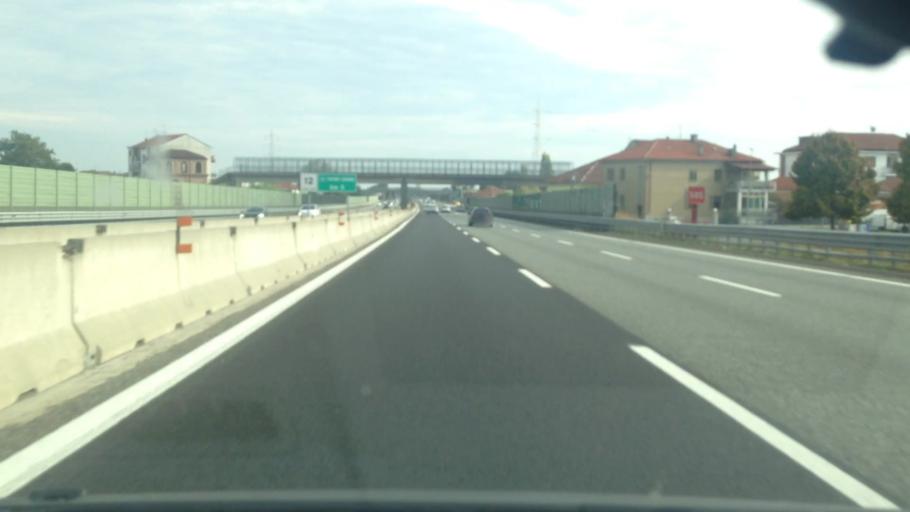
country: IT
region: Piedmont
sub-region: Provincia di Torino
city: Nichelino
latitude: 44.9847
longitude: 7.6407
